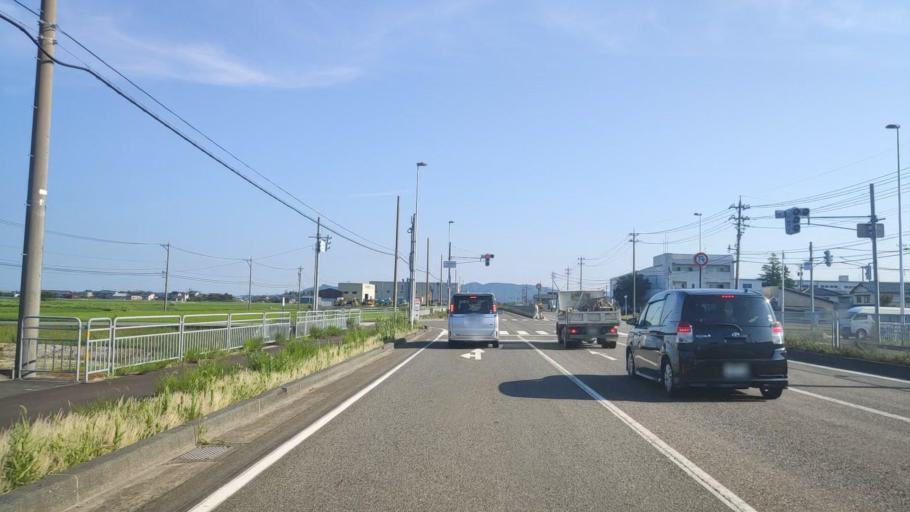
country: JP
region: Fukui
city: Maruoka
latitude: 36.1634
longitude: 136.2636
